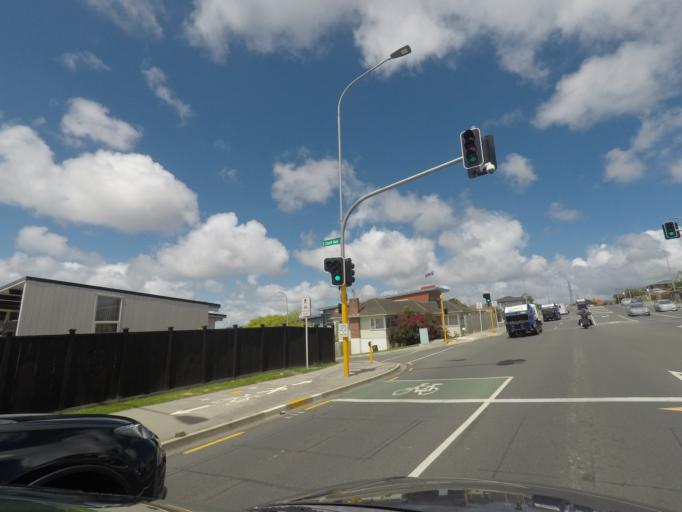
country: NZ
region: Auckland
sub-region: Auckland
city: Rosebank
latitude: -36.8600
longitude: 174.6512
